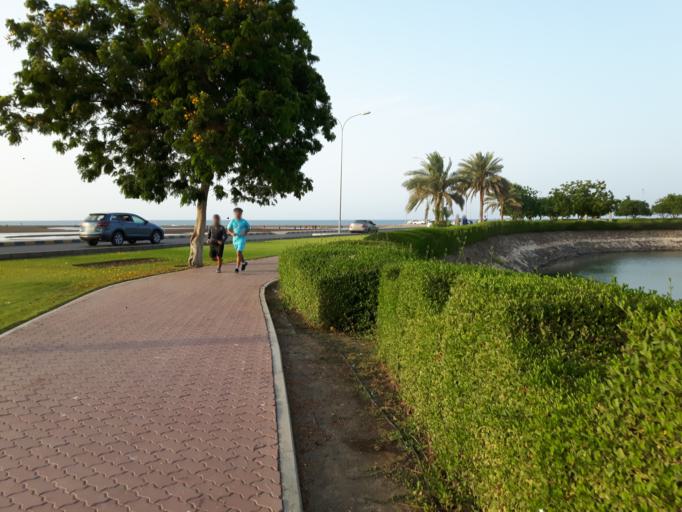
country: OM
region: Al Batinah
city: Al Sohar
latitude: 24.4076
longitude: 56.7163
